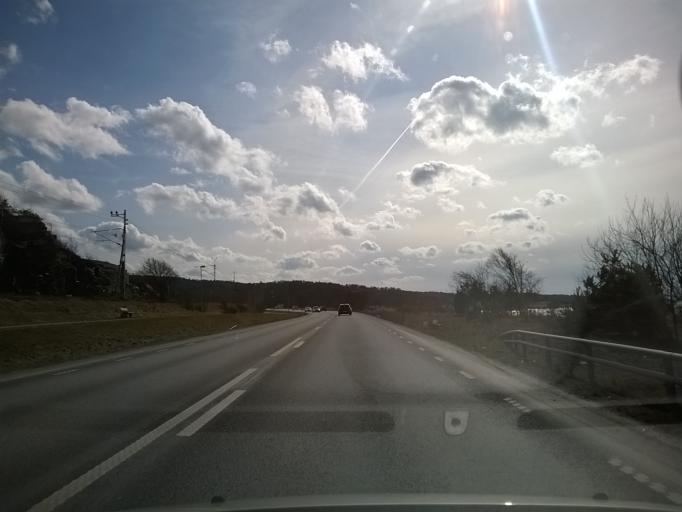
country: SE
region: Vaestra Goetaland
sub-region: Stenungsunds Kommun
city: Stora Hoga
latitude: 58.0393
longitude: 11.8212
